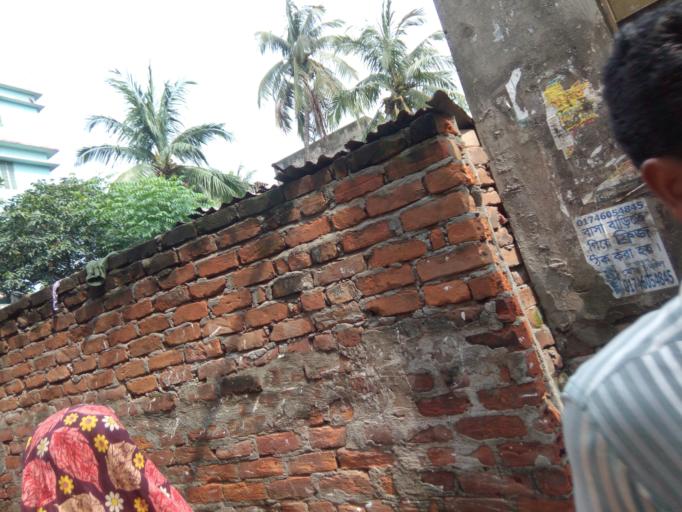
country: BD
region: Dhaka
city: Azimpur
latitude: 23.7387
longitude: 90.3647
